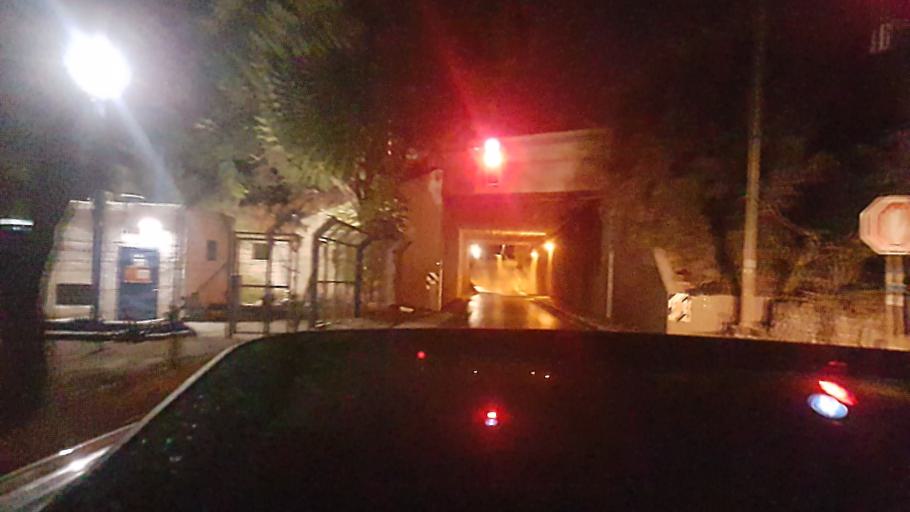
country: IL
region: Central District
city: Hod HaSharon
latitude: 32.1625
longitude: 34.8784
